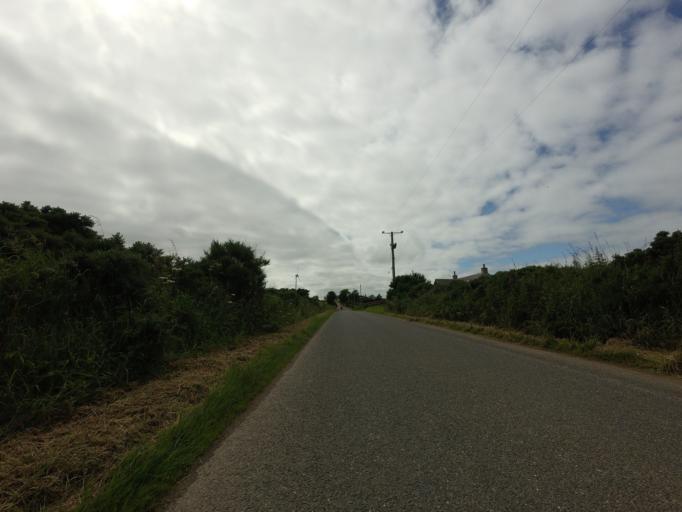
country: GB
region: Scotland
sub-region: Aberdeenshire
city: Turriff
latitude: 57.5451
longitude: -2.2845
